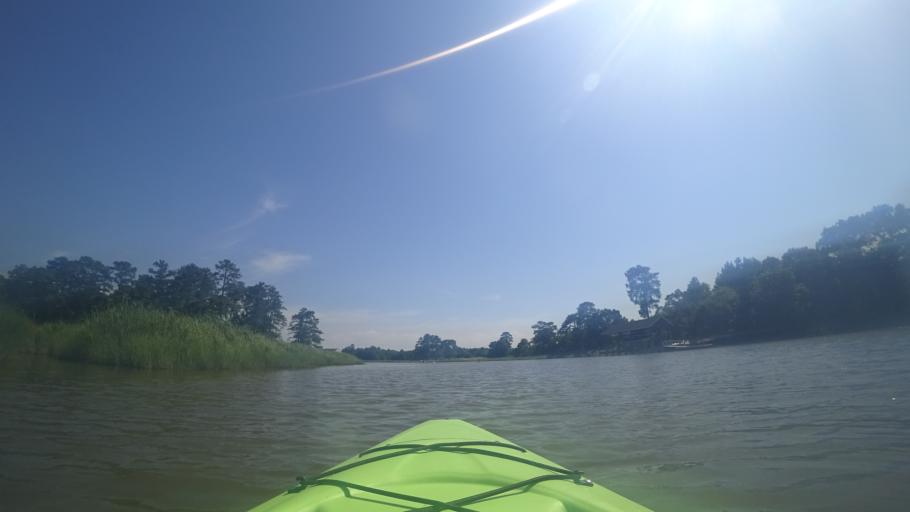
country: US
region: Virginia
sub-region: Isle of Wight County
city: Smithfield
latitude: 36.9557
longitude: -76.6165
